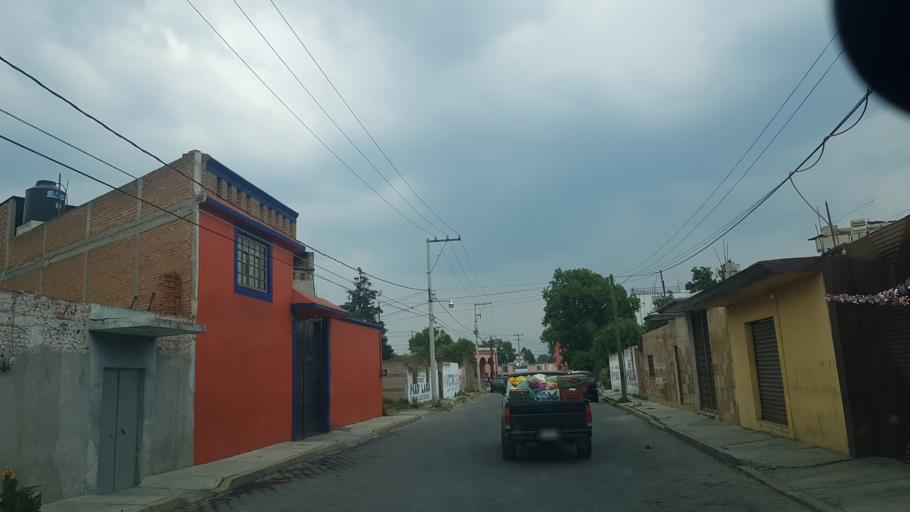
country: MX
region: Puebla
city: Huejotzingo
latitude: 19.1666
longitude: -98.4106
